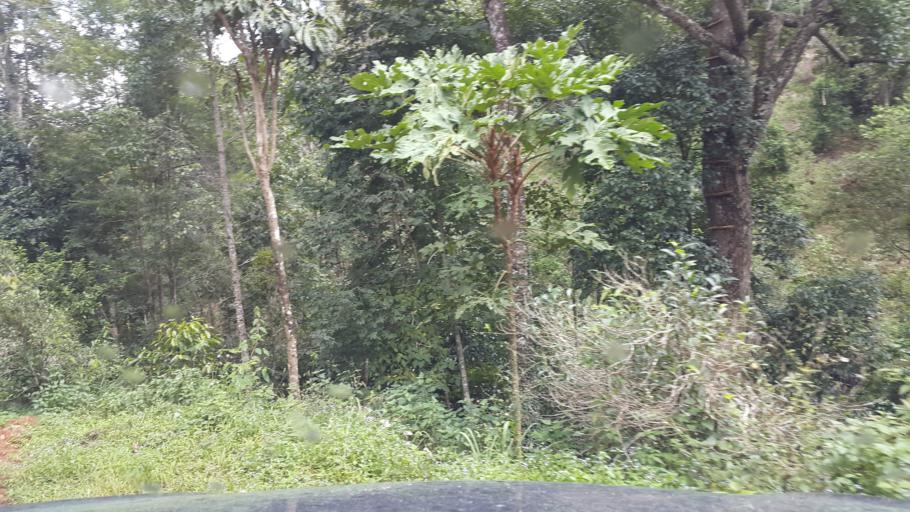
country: TH
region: Lampang
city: Wang Nuea
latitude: 19.1153
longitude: 99.3646
